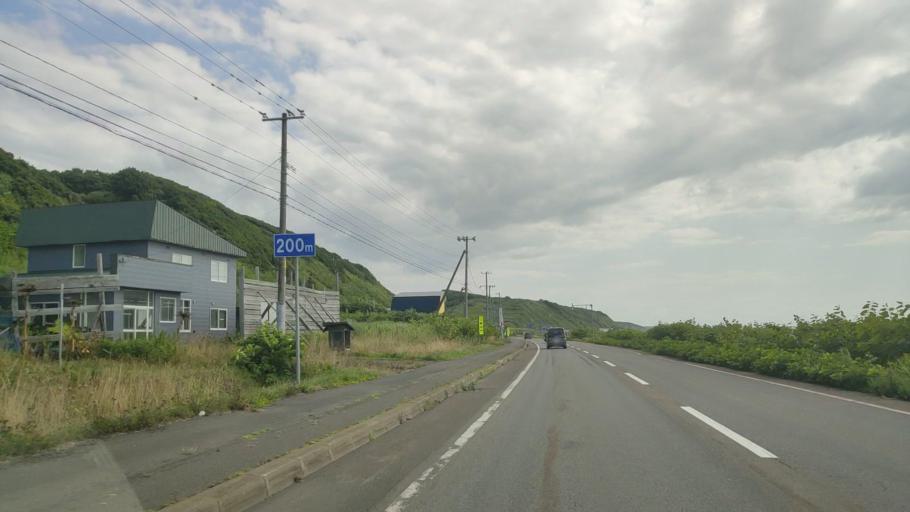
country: JP
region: Hokkaido
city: Rumoi
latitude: 44.2070
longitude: 141.6573
